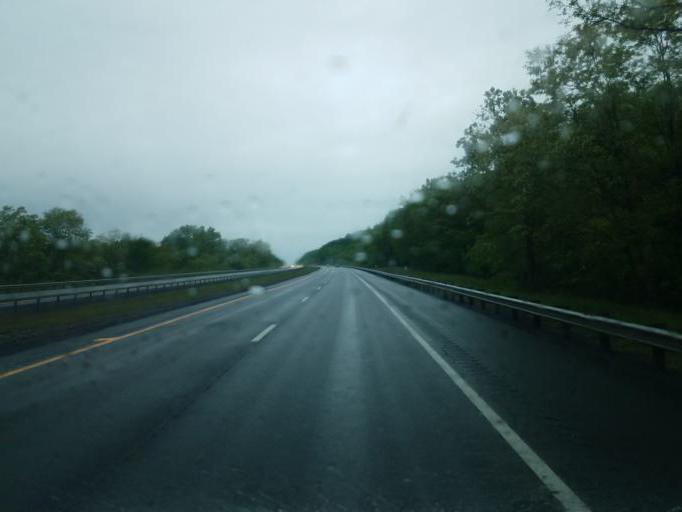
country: US
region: New York
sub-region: Herkimer County
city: Ilion
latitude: 43.0226
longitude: -75.0212
